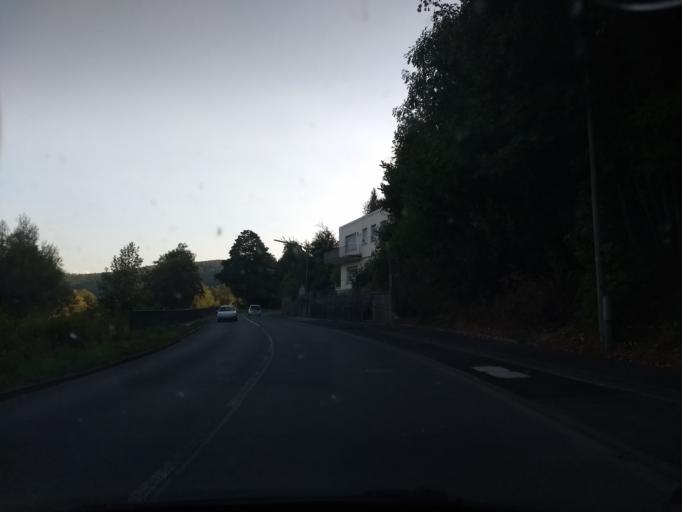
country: DE
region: North Rhine-Westphalia
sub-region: Regierungsbezirk Arnsberg
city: Arnsberg
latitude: 51.3972
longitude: 8.0559
